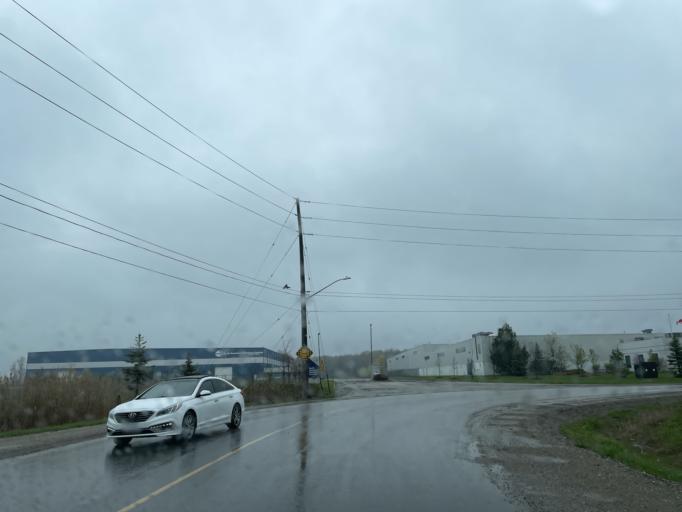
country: CA
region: Ontario
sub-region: Wellington County
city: Guelph
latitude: 43.5455
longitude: -80.3085
